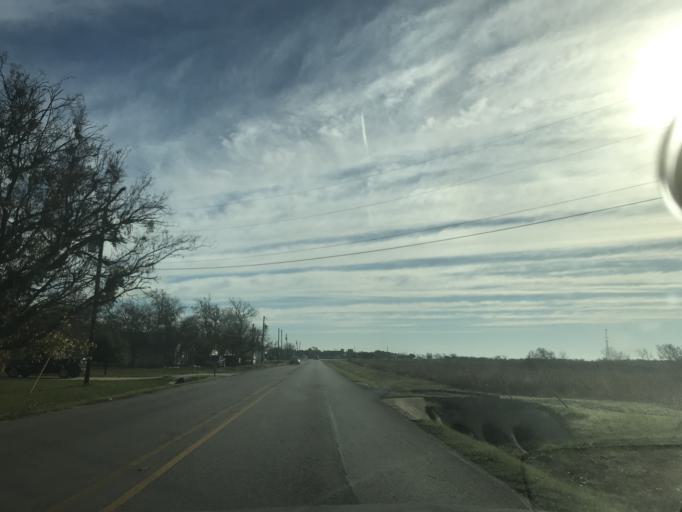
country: US
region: Texas
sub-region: Travis County
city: Manor
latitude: 30.3375
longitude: -97.5573
